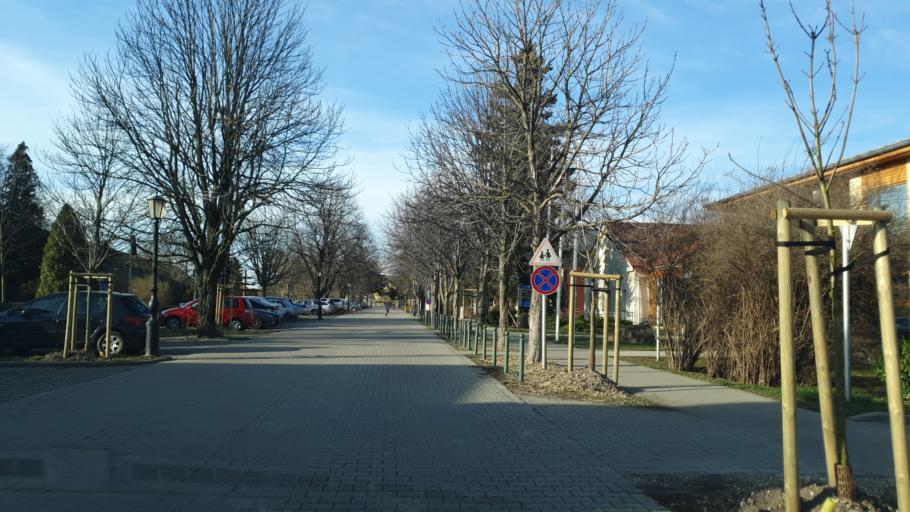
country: HU
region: Fejer
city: Etyek
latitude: 47.5012
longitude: 18.7523
